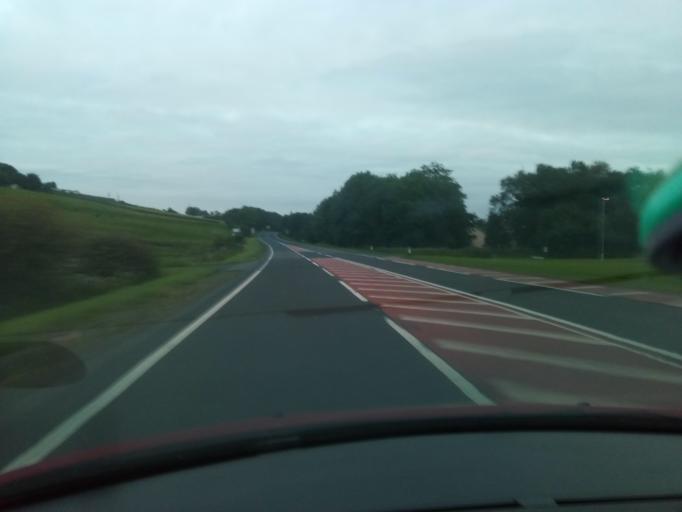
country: GB
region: England
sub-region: Northumberland
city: Bardon Mill
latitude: 54.9757
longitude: -2.3597
